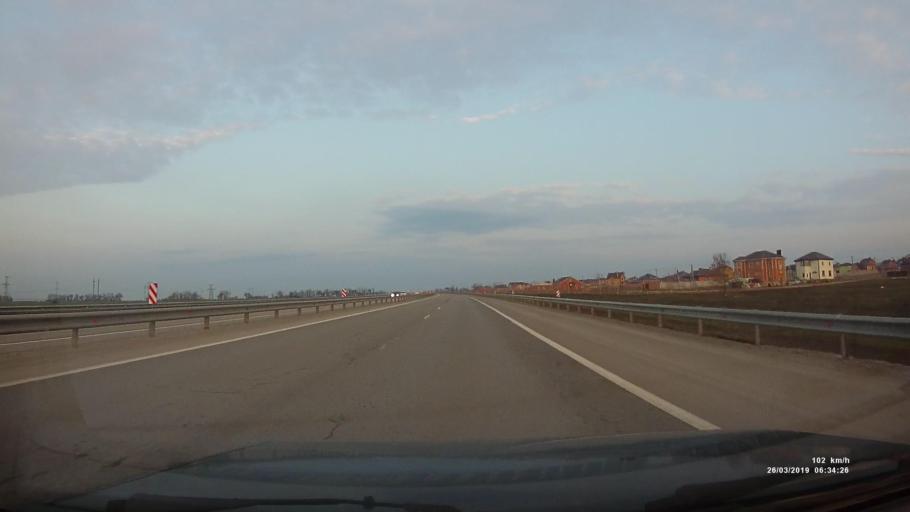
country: RU
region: Rostov
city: Chaltyr
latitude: 47.2767
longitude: 39.4667
